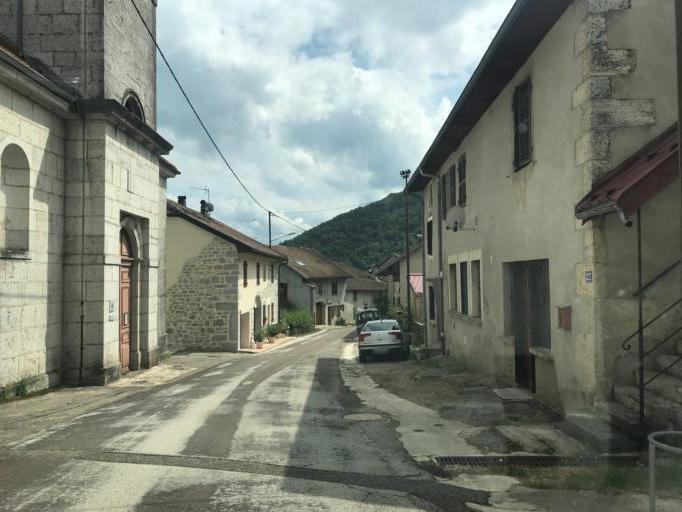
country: FR
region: Franche-Comte
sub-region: Departement du Jura
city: Valfin-les-Saint-Claude
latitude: 46.4388
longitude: 5.8552
